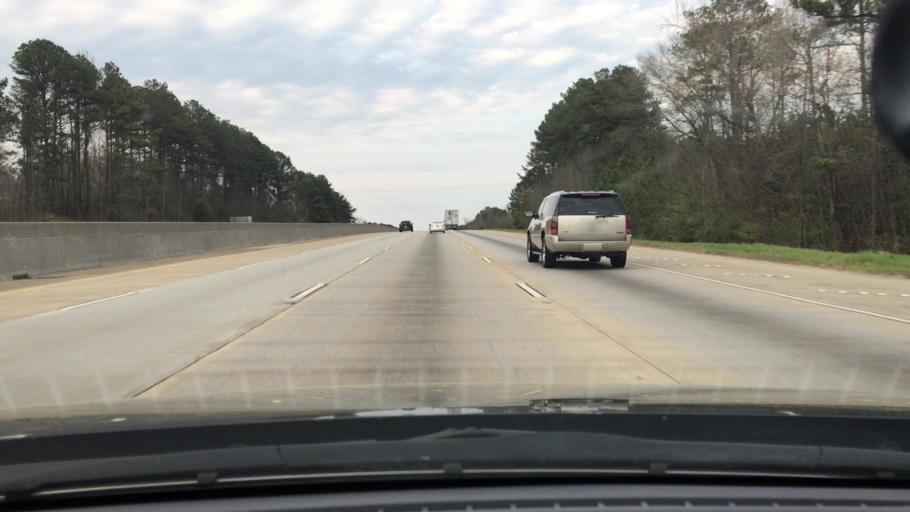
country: US
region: Georgia
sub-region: Coweta County
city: Newnan
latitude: 33.4165
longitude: -84.7315
